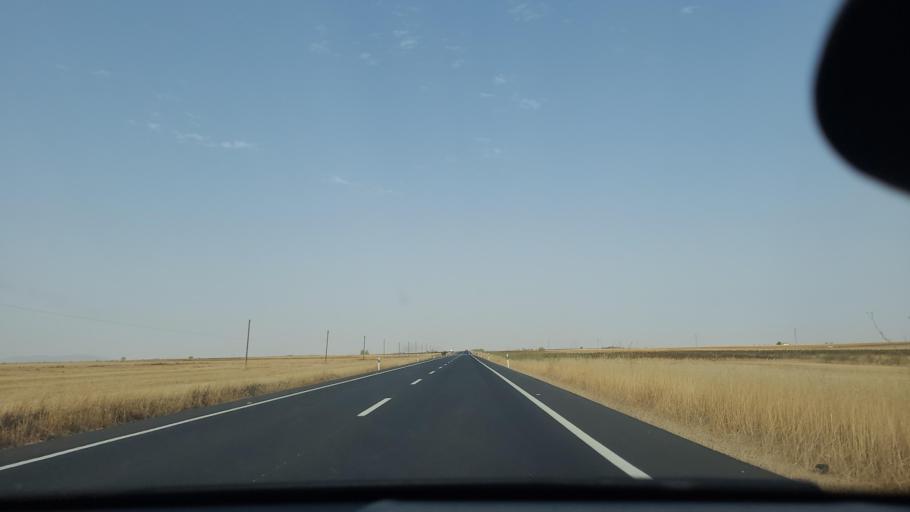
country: ES
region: Extremadura
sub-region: Provincia de Badajoz
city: Azuaga
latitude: 38.2623
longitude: -5.7314
